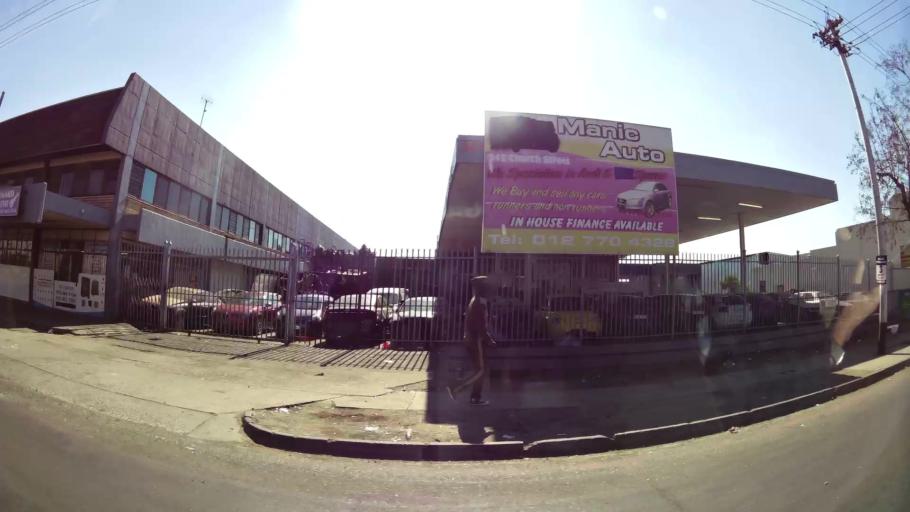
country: ZA
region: Gauteng
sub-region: City of Tshwane Metropolitan Municipality
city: Pretoria
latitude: -25.7490
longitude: 28.1508
